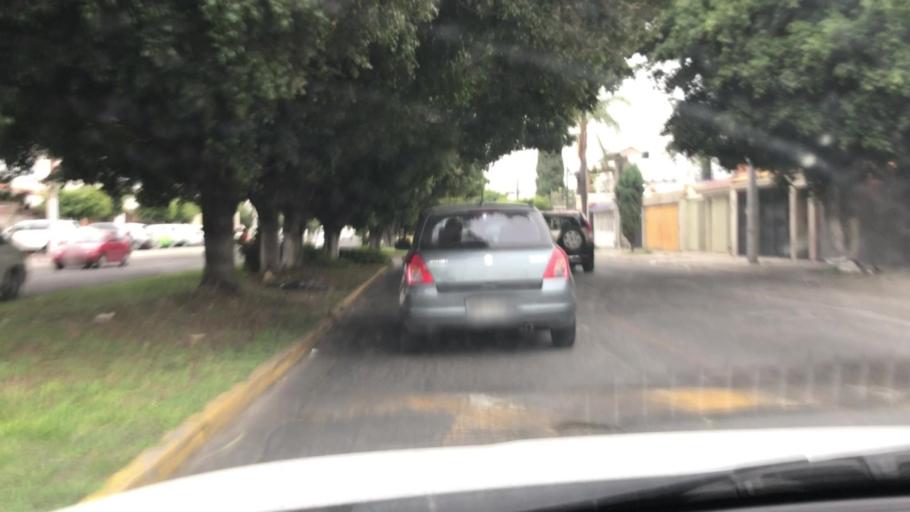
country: MX
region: Jalisco
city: Guadalajara
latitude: 20.6525
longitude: -103.4255
